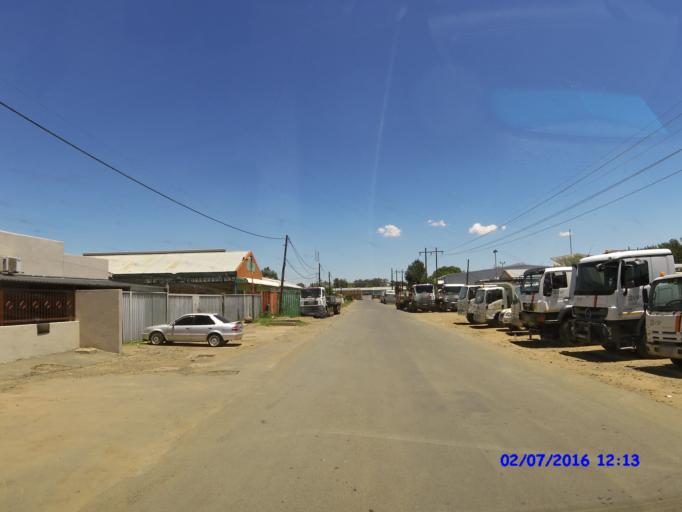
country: LS
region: Maseru
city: Maseru
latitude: -29.2960
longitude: 27.4754
